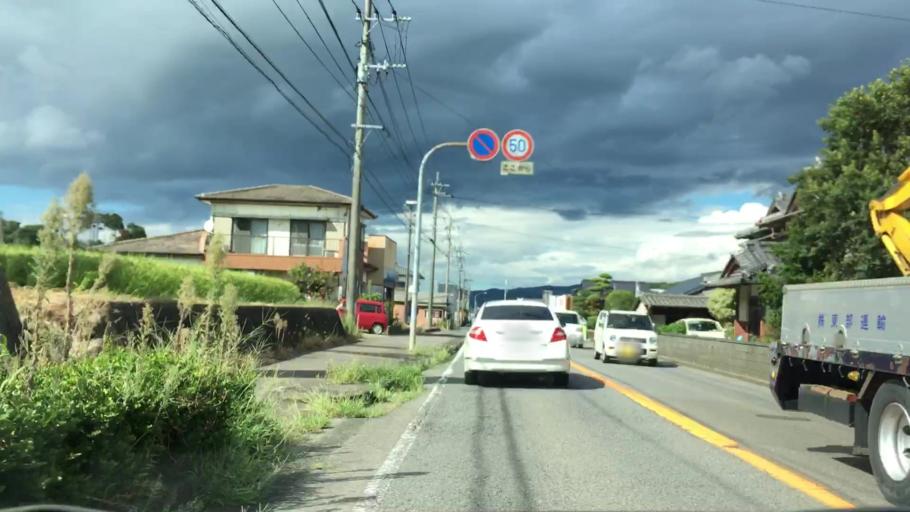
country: JP
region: Saga Prefecture
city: Imaricho-ko
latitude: 33.2432
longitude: 129.8505
